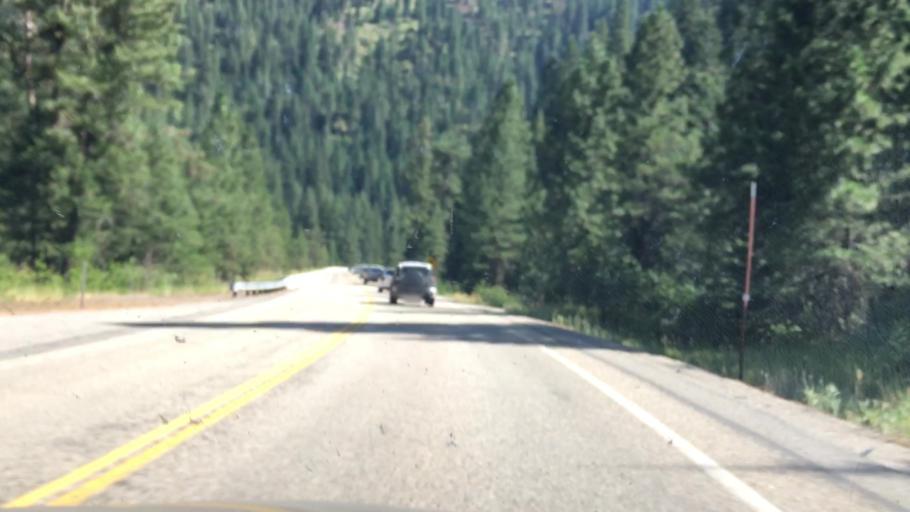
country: US
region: Idaho
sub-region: Valley County
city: Cascade
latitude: 44.1810
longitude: -116.1165
